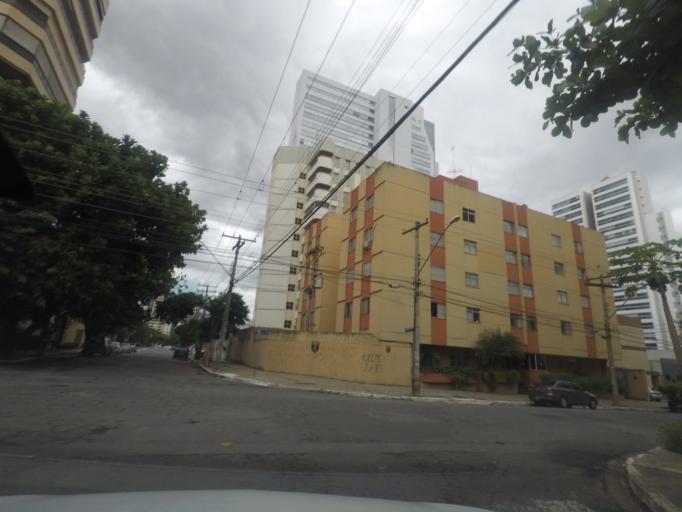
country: BR
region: Goias
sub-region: Goiania
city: Goiania
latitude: -16.6837
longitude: -49.2636
